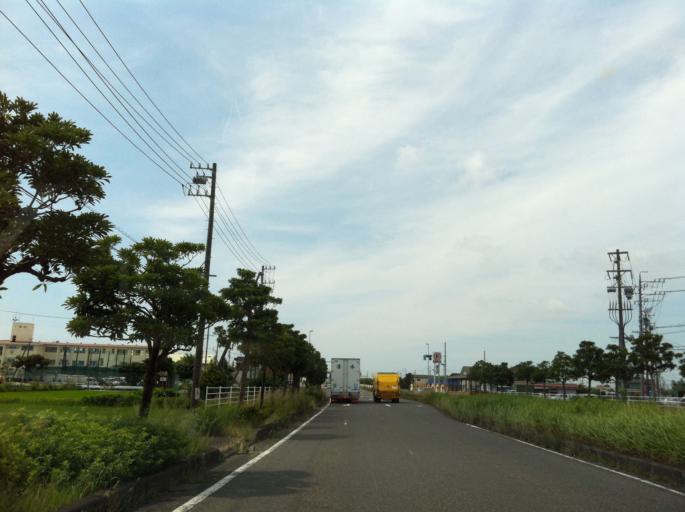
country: JP
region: Shizuoka
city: Yaizu
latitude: 34.8526
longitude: 138.2995
